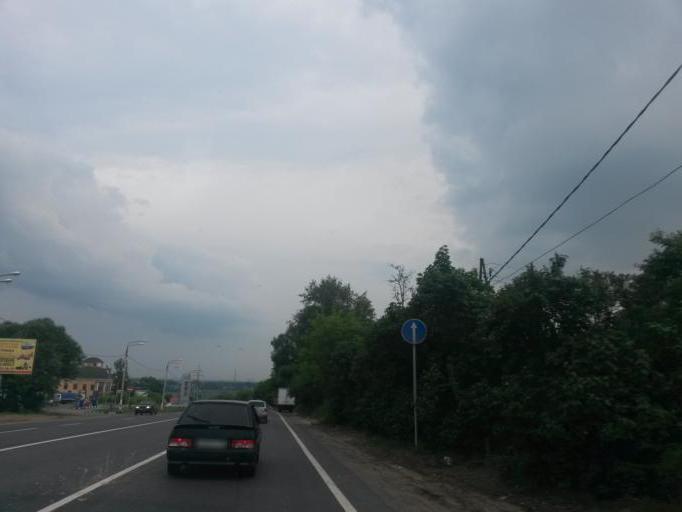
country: RU
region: Moskovskaya
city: Yam
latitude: 55.5044
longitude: 37.7517
